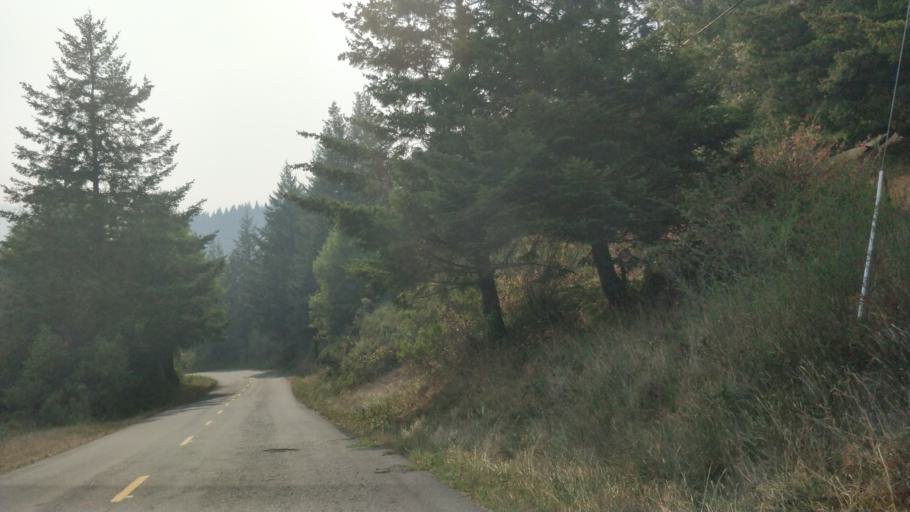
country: US
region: California
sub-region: Humboldt County
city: Rio Dell
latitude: 40.2939
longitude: -124.2499
